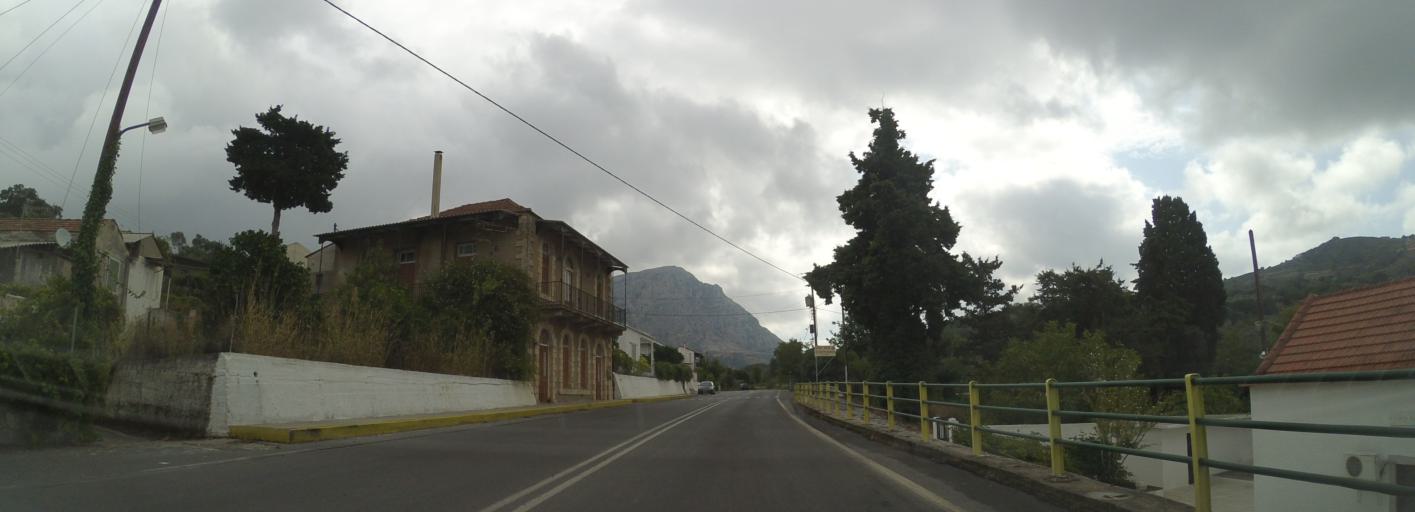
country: GR
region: Crete
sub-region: Nomos Rethymnis
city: Agia Foteini
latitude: 35.2203
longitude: 24.5200
